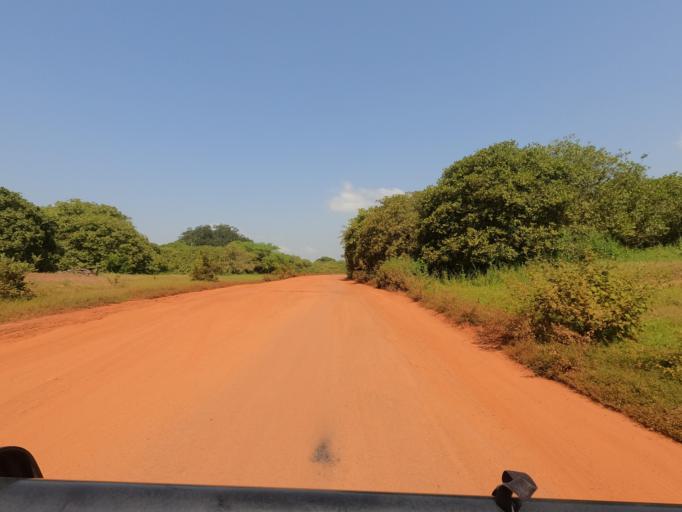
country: GW
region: Cacheu
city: Canchungo
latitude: 12.2683
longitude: -15.7877
